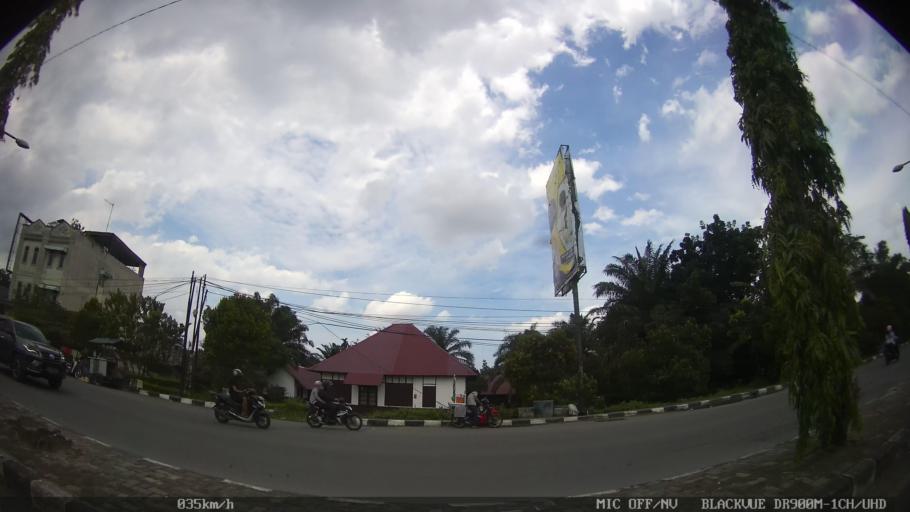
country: ID
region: North Sumatra
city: Medan
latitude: 3.6280
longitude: 98.6631
